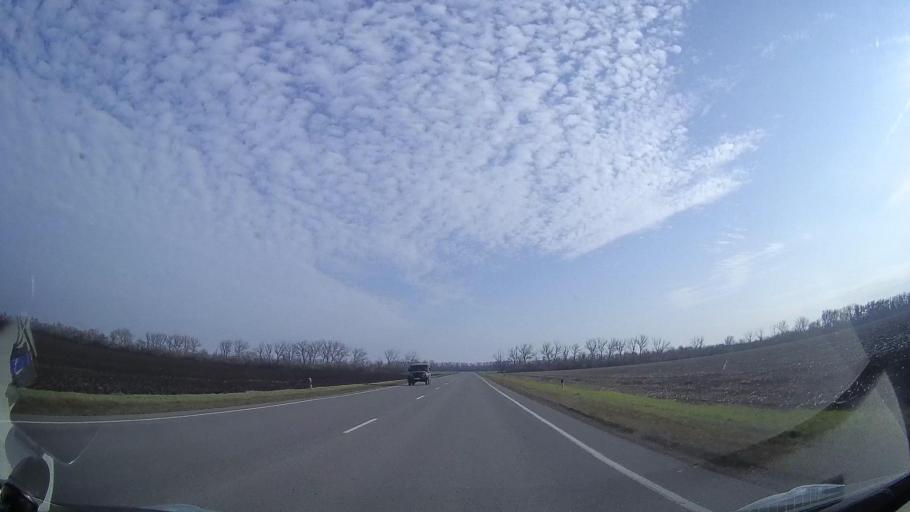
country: RU
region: Rostov
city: Tselina
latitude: 46.5216
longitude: 41.1462
